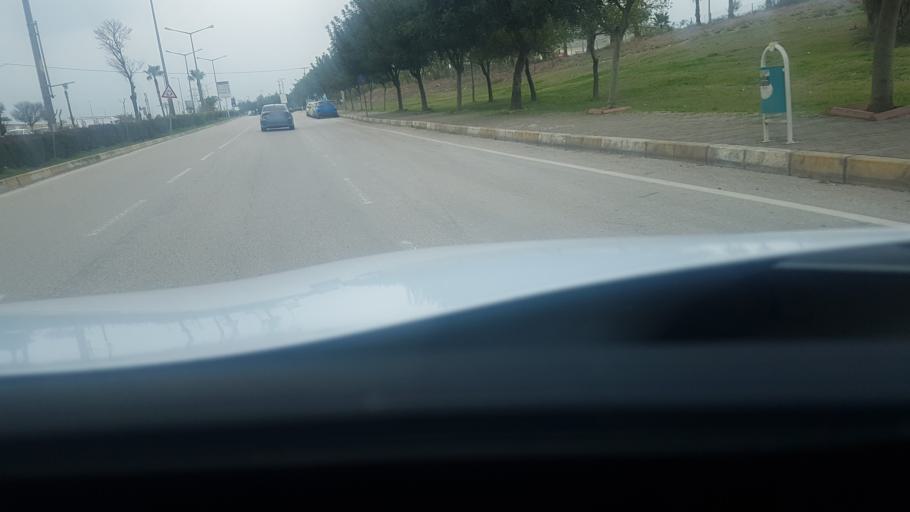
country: TR
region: Adana
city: Seyhan
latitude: 37.0548
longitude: 35.2494
